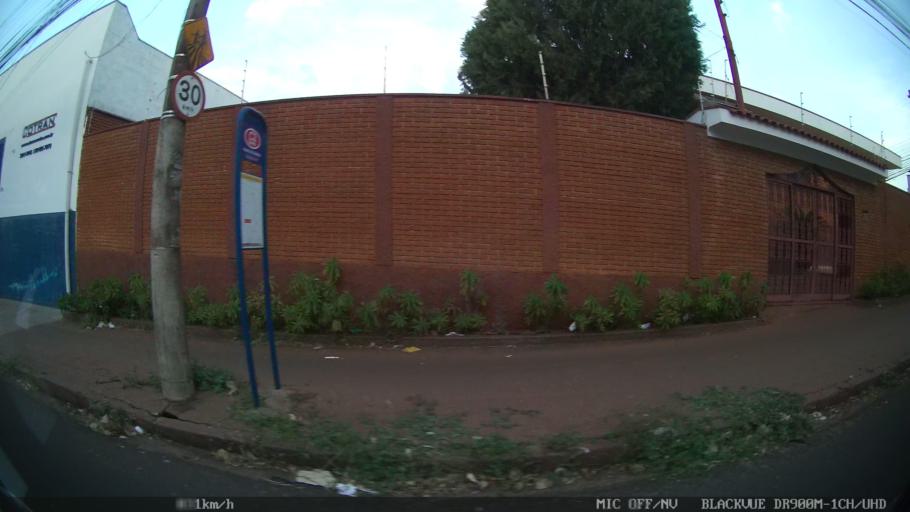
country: BR
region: Sao Paulo
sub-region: Ribeirao Preto
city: Ribeirao Preto
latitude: -21.1554
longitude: -47.8279
